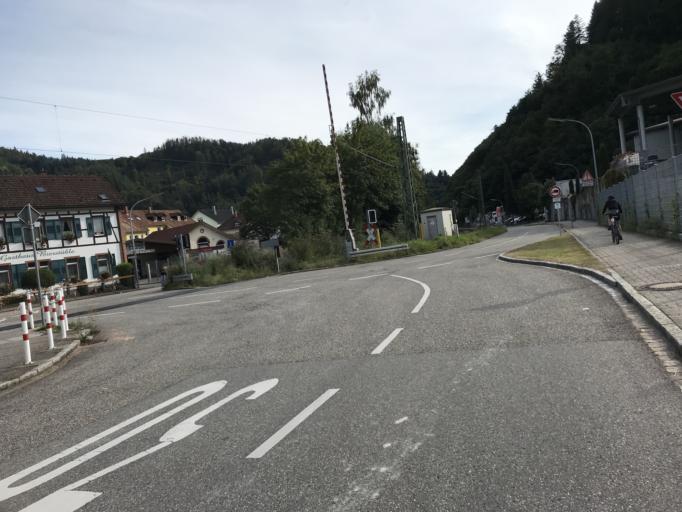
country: DE
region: Baden-Wuerttemberg
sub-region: Freiburg Region
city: Zell im Wiesental
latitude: 47.7042
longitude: 7.8465
